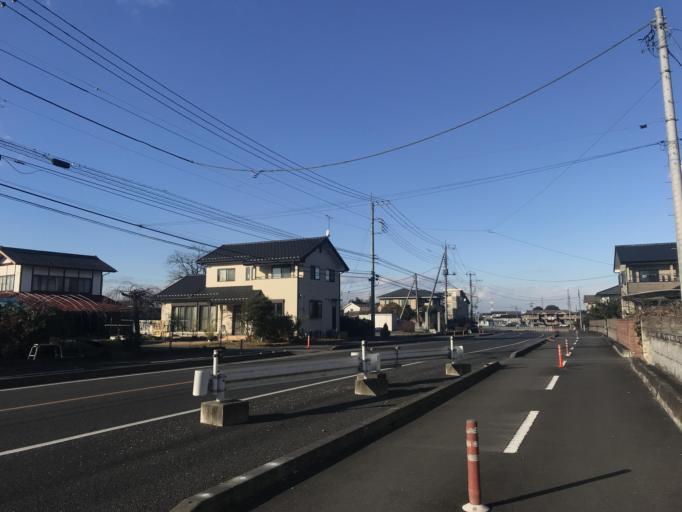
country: JP
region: Tochigi
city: Kaminokawa
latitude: 36.4316
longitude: 139.8718
